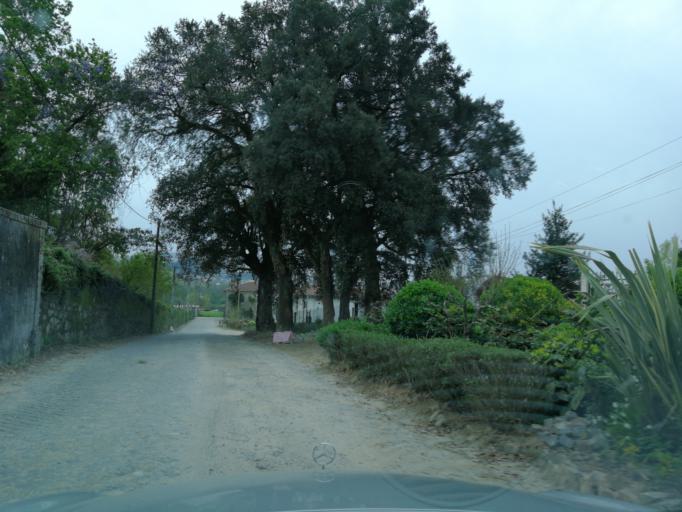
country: PT
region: Braga
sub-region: Braga
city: Braga
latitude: 41.5803
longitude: -8.4403
